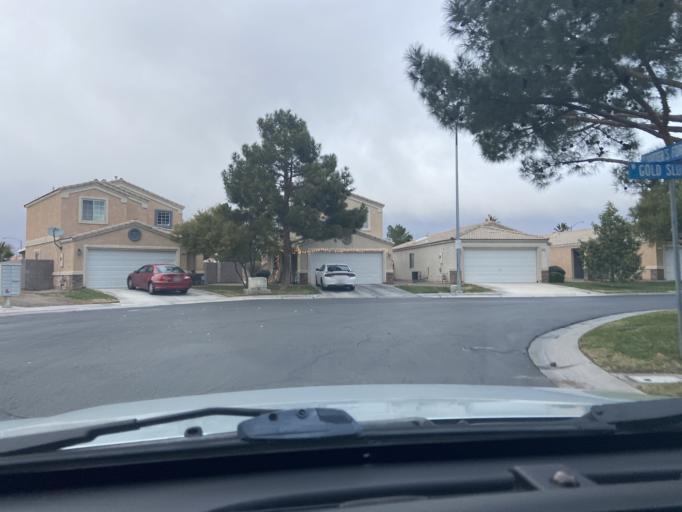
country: US
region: Nevada
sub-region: Clark County
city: Las Vegas
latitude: 36.2205
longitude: -115.1881
